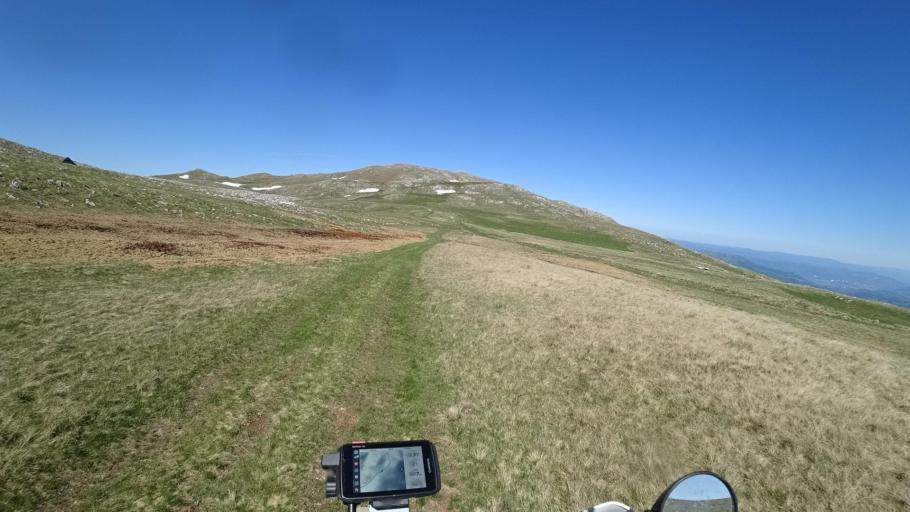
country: BA
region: Federation of Bosnia and Herzegovina
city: Travnik
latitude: 44.2802
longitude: 17.6518
